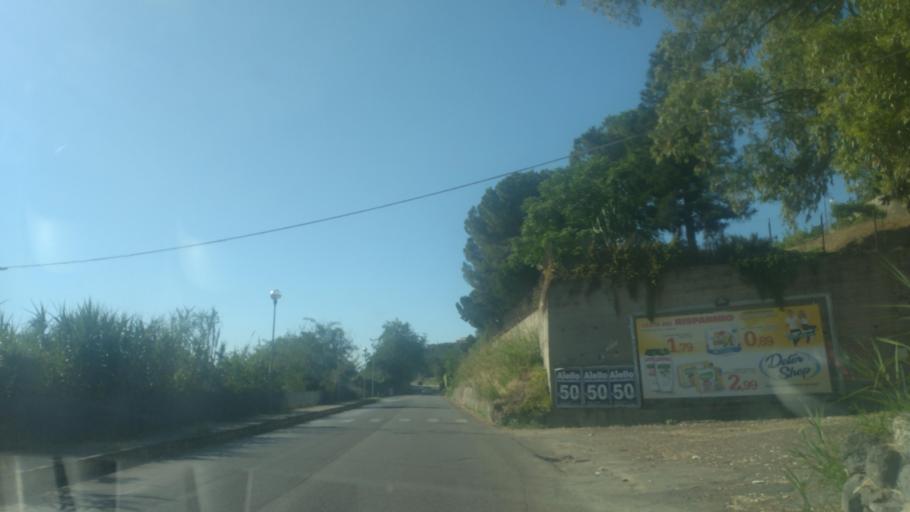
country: IT
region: Calabria
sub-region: Provincia di Catanzaro
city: Soverato Superiore
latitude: 38.7019
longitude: 16.5361
